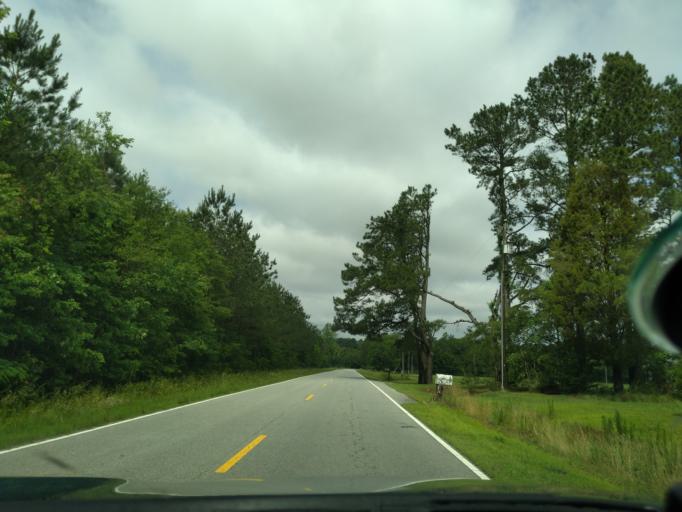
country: US
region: North Carolina
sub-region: Chowan County
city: Edenton
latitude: 35.9254
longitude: -76.5922
